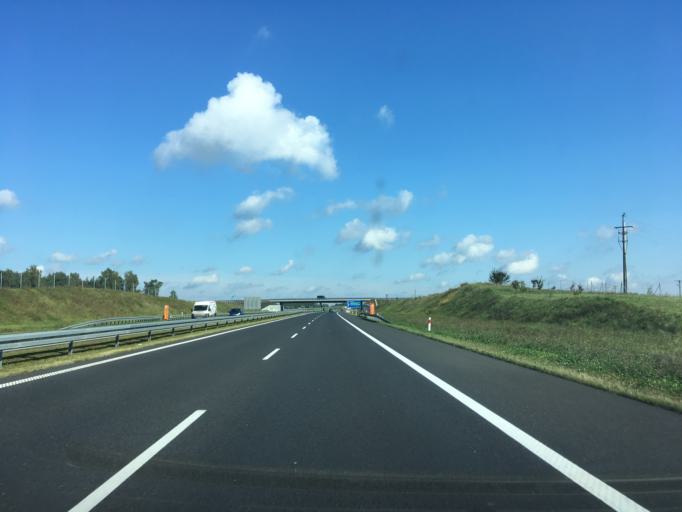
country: PL
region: Kujawsko-Pomorskie
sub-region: Powiat swiecki
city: Warlubie
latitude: 53.5963
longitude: 18.6164
